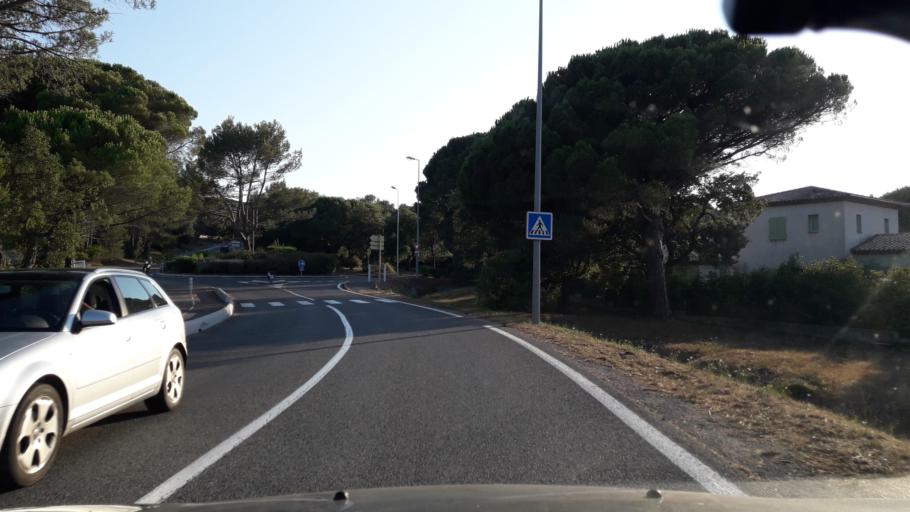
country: FR
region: Provence-Alpes-Cote d'Azur
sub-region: Departement du Var
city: Saint-Raphael
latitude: 43.4493
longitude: 6.8173
